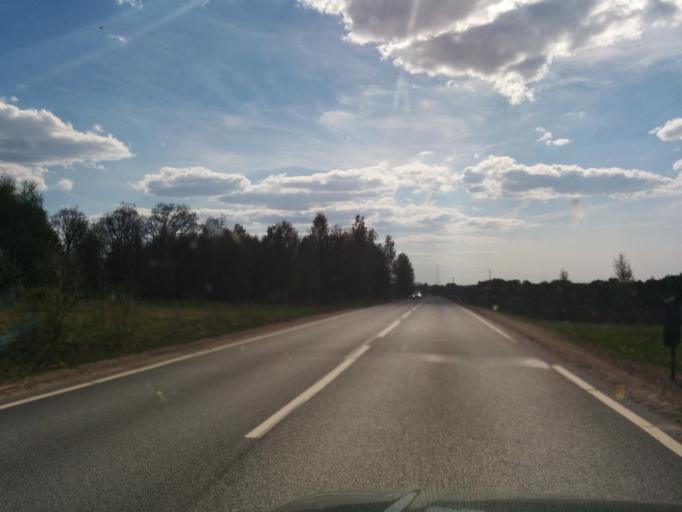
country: LV
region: Sigulda
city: Sigulda
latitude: 57.2302
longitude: 24.8099
